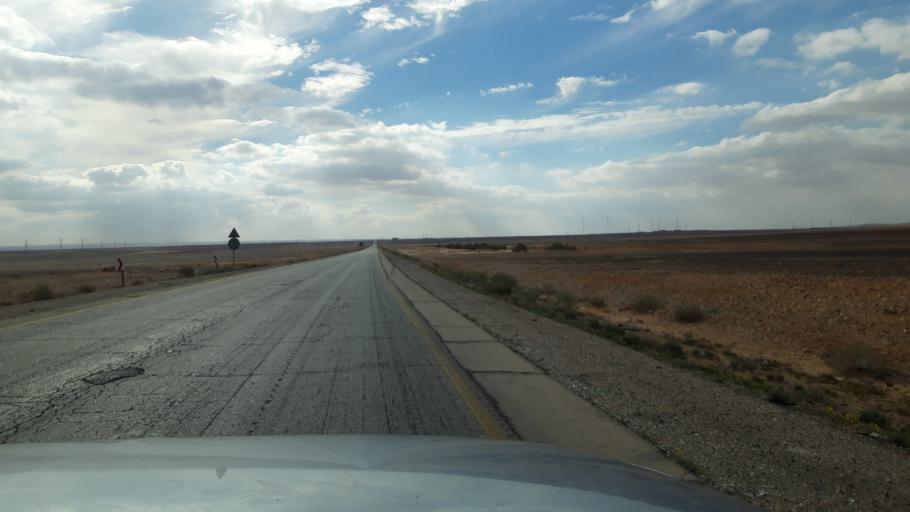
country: JO
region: Amman
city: Al Azraq ash Shamali
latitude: 31.7317
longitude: 36.5055
